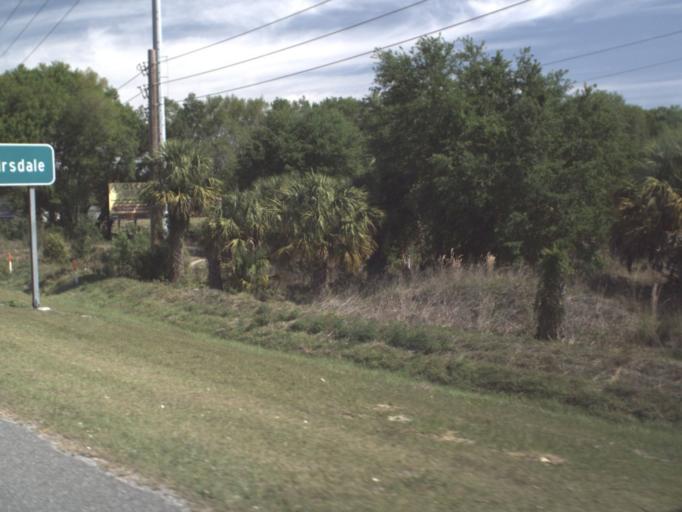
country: US
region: Florida
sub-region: Lake County
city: Lady Lake
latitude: 28.9203
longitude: -81.9240
